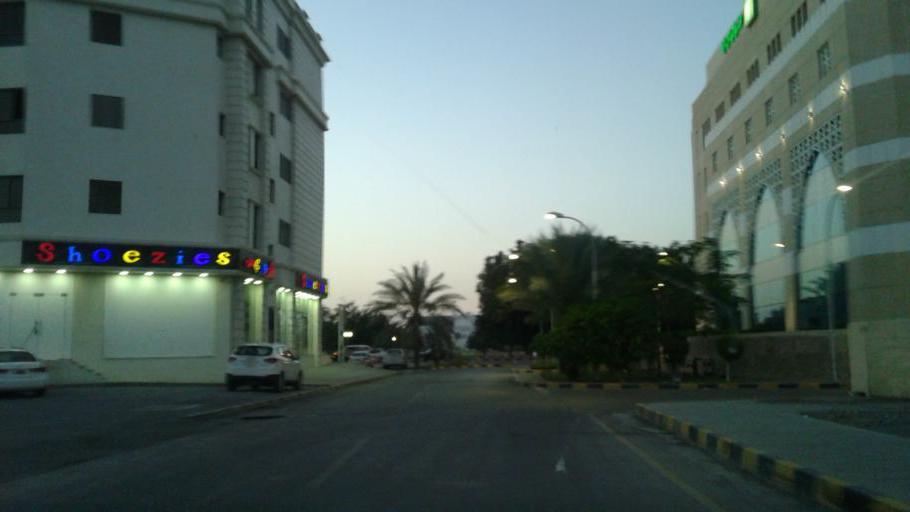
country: OM
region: Muhafazat Masqat
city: As Sib al Jadidah
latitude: 23.6107
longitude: 58.2436
